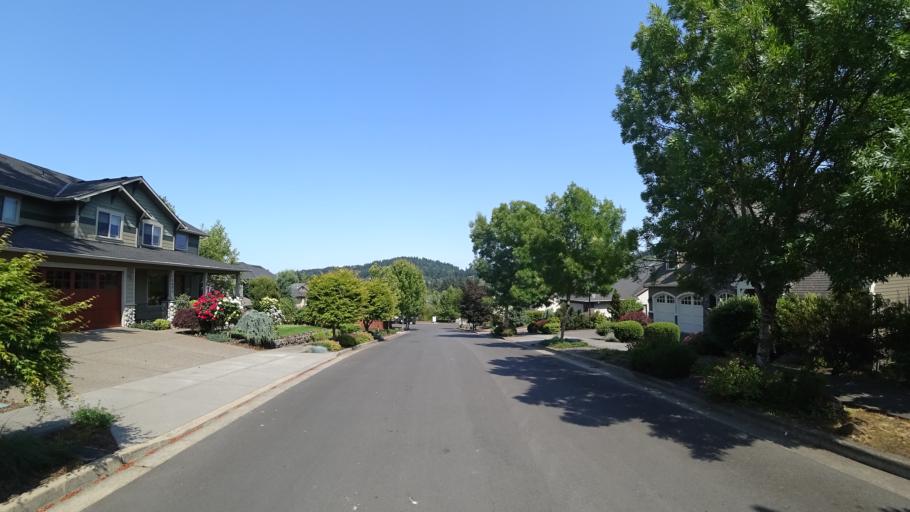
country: US
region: Oregon
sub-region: Clackamas County
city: Happy Valley
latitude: 45.4442
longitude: -122.5357
